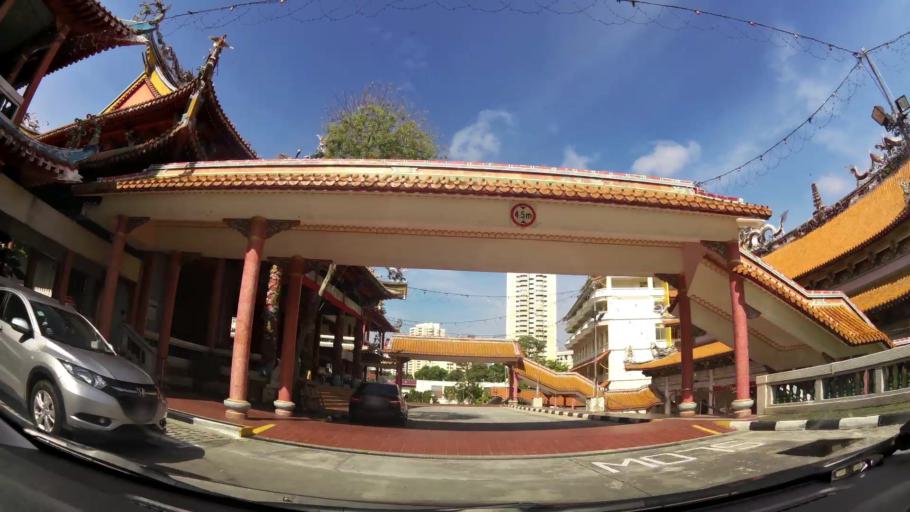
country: SG
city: Singapore
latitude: 1.3618
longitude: 103.8367
